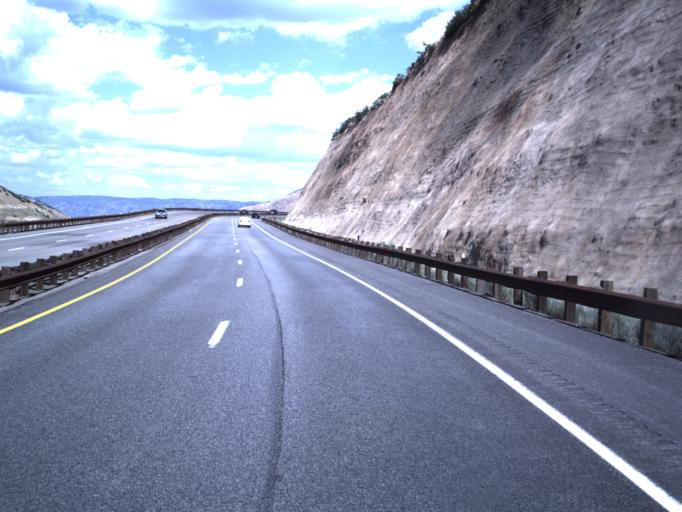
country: US
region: Utah
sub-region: Wasatch County
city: Midway
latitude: 40.4061
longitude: -111.5225
